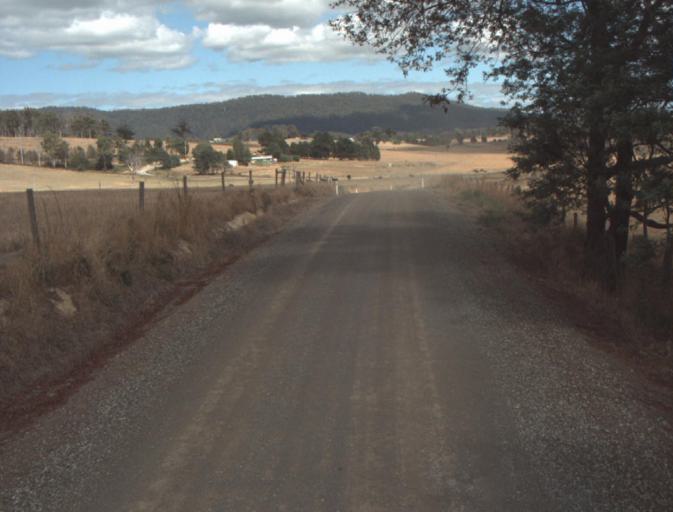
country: AU
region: Tasmania
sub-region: Launceston
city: Mayfield
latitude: -41.2187
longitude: 147.1636
